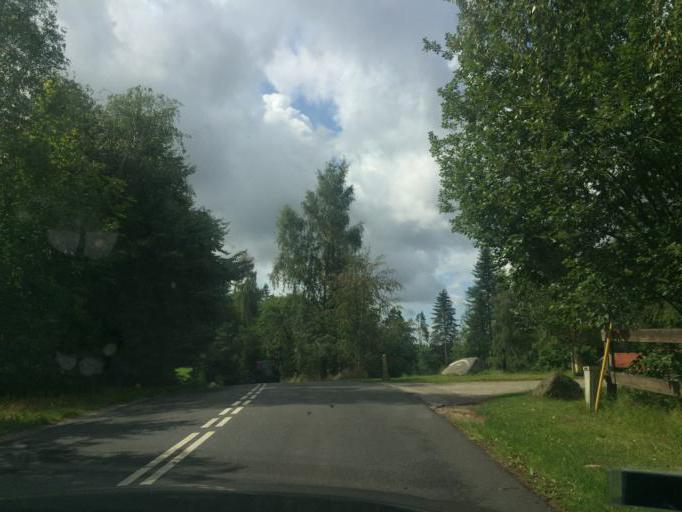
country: DK
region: Capital Region
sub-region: Allerod Kommune
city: Blovstrod
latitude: 55.8444
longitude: 12.3874
